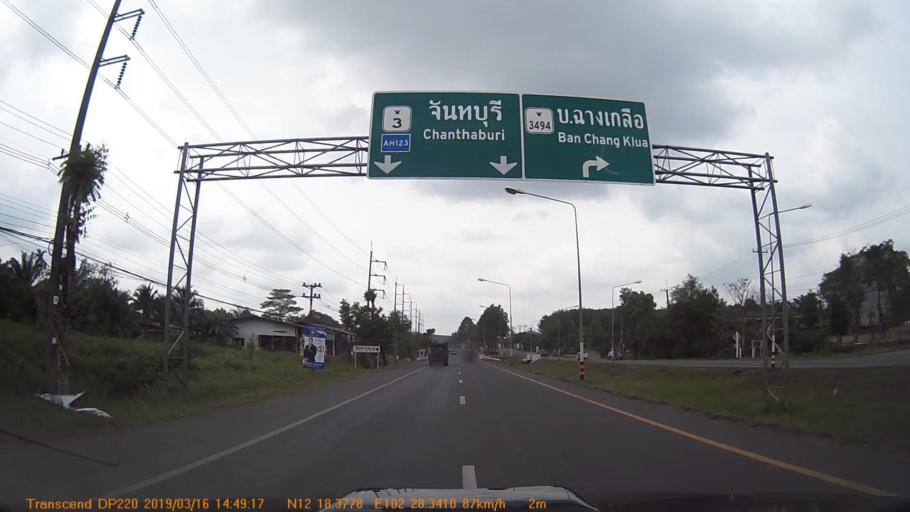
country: TH
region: Trat
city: Khao Saming
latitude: 12.3065
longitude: 102.4722
